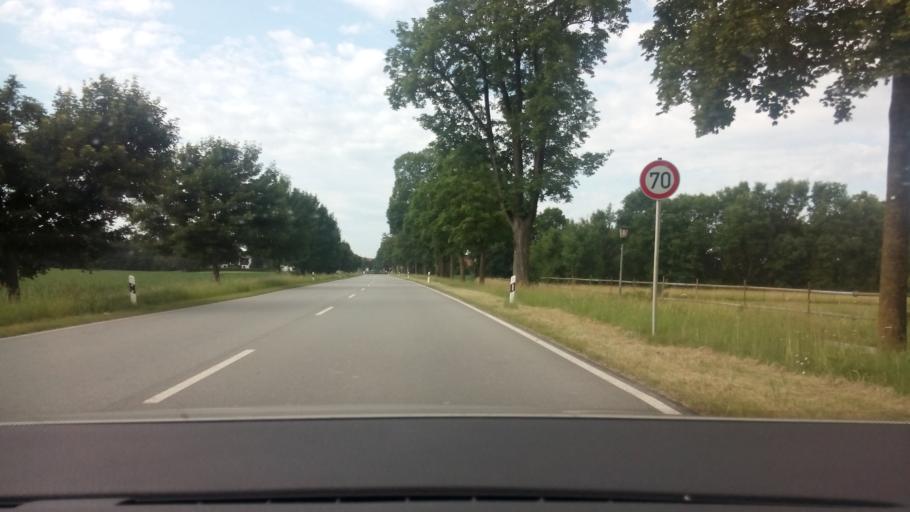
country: DE
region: Bavaria
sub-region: Upper Bavaria
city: Garching bei Munchen
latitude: 48.2368
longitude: 11.6421
